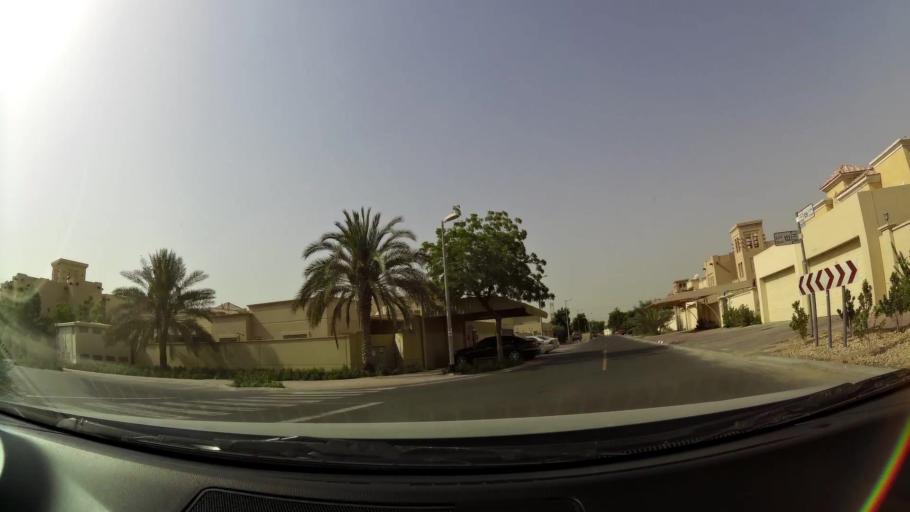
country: AE
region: Ash Shariqah
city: Sharjah
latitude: 25.2686
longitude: 55.4577
